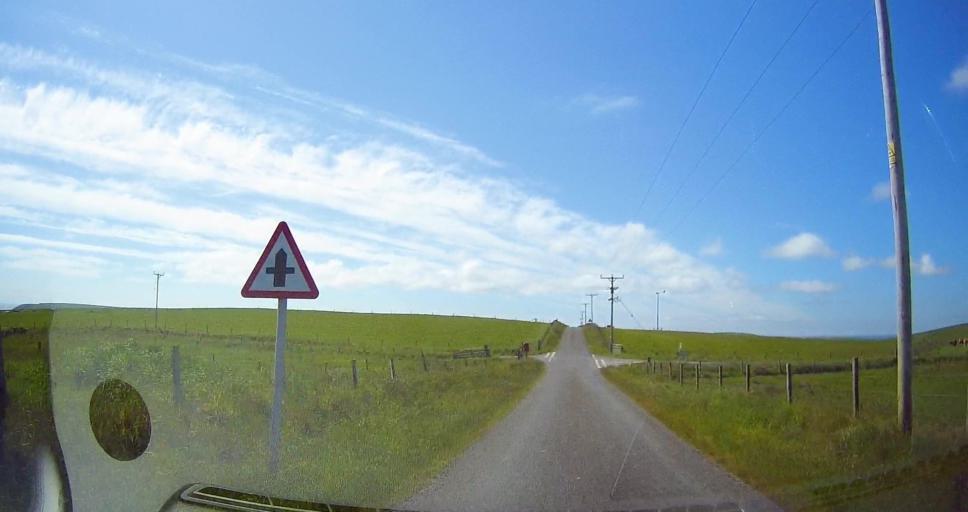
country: GB
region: Scotland
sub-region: Orkney Islands
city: Orkney
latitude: 58.8101
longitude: -2.9294
